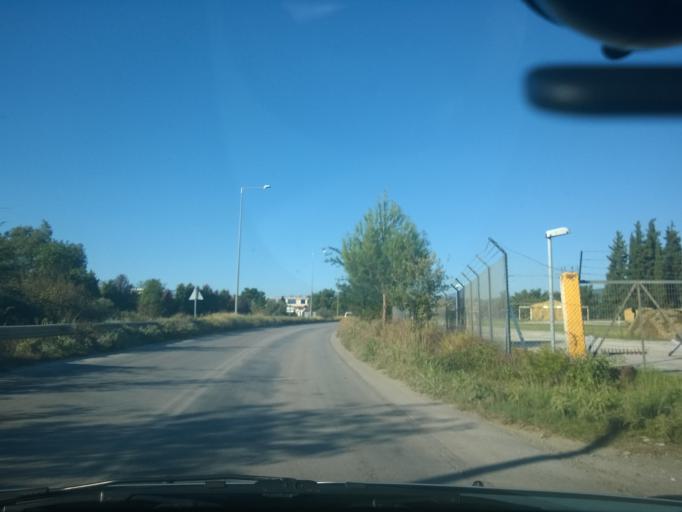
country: GR
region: Central Macedonia
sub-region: Nomos Thessalonikis
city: Thermi
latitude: 40.5332
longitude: 23.0141
